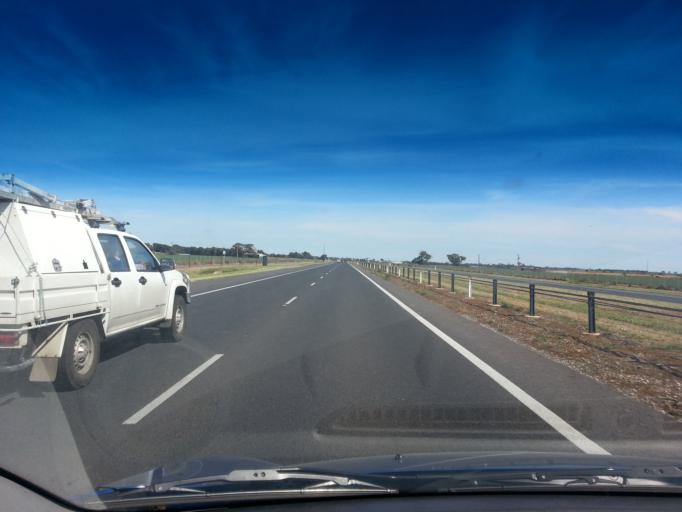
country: AU
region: South Australia
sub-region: Gawler
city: Gawler
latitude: -34.6034
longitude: 138.7049
